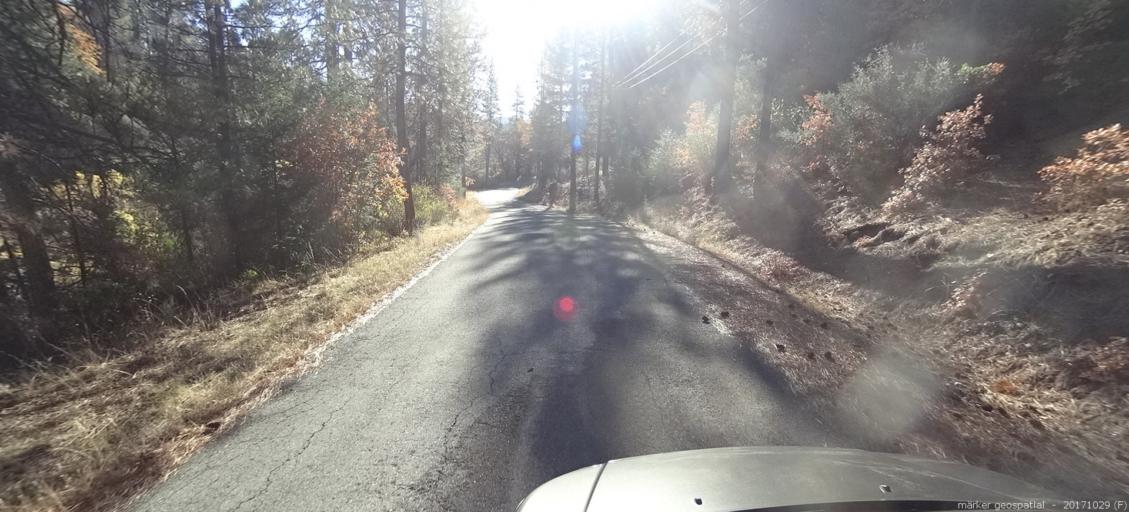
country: US
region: California
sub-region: Trinity County
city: Hayfork
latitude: 40.3653
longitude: -122.9694
